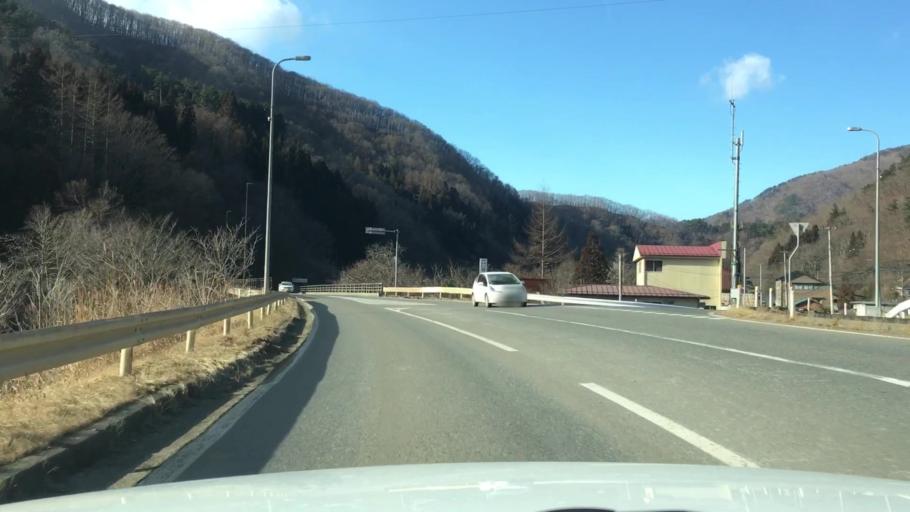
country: JP
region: Iwate
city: Tono
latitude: 39.6149
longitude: 141.6273
